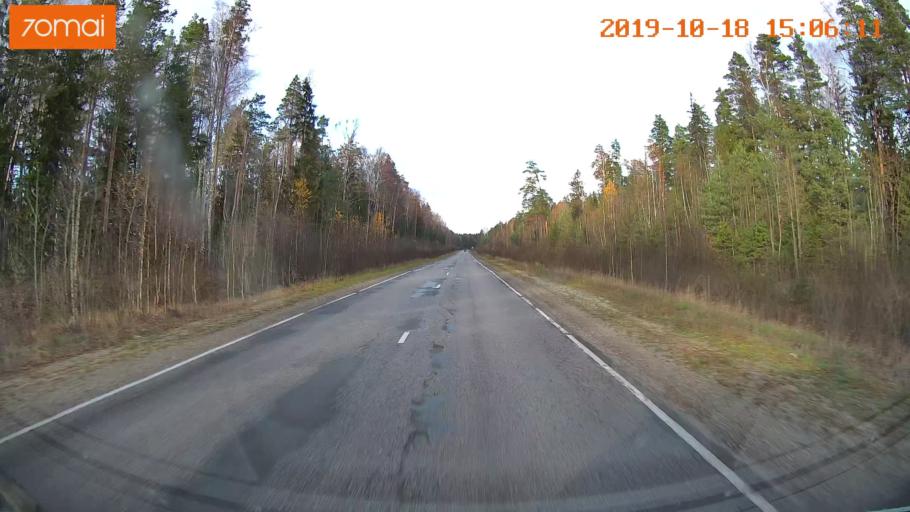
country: RU
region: Vladimir
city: Gus'-Khrustal'nyy
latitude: 55.5262
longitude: 40.5768
